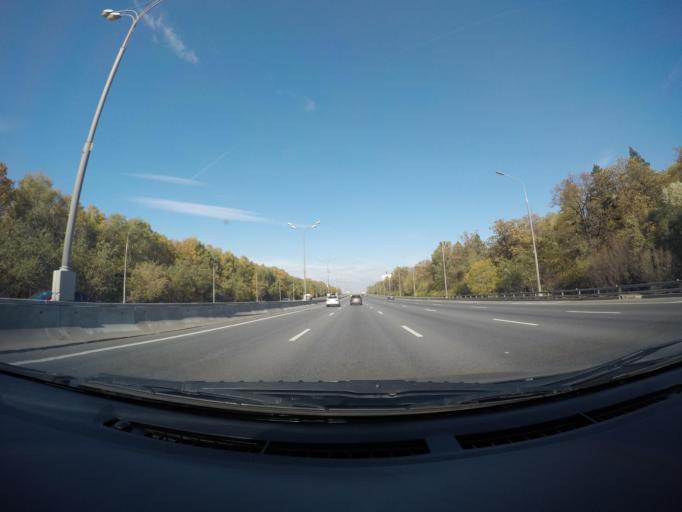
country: RU
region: Moscow
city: Ivanovskoye
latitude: 55.7949
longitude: 37.8409
